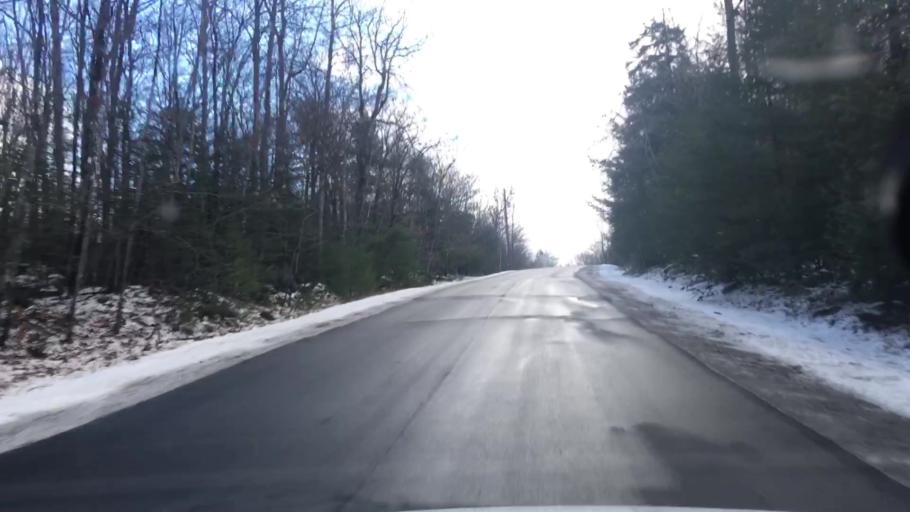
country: US
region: Maine
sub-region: Hancock County
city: Dedham
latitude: 44.6871
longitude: -68.7130
